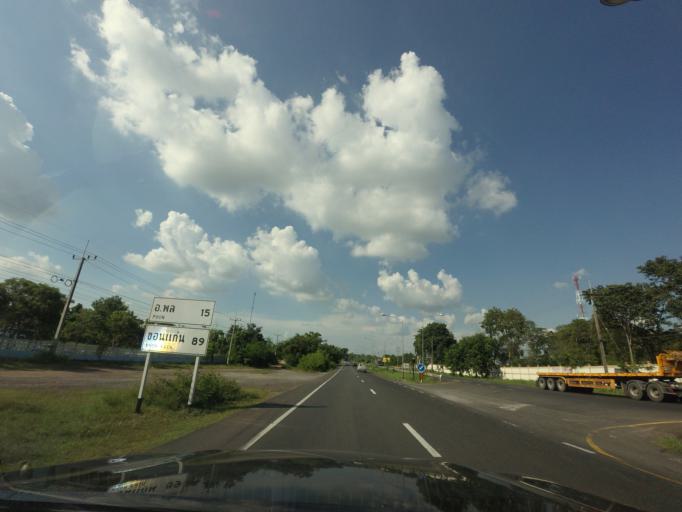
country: TH
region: Nakhon Ratchasima
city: Bua Lai
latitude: 15.6791
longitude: 102.5767
